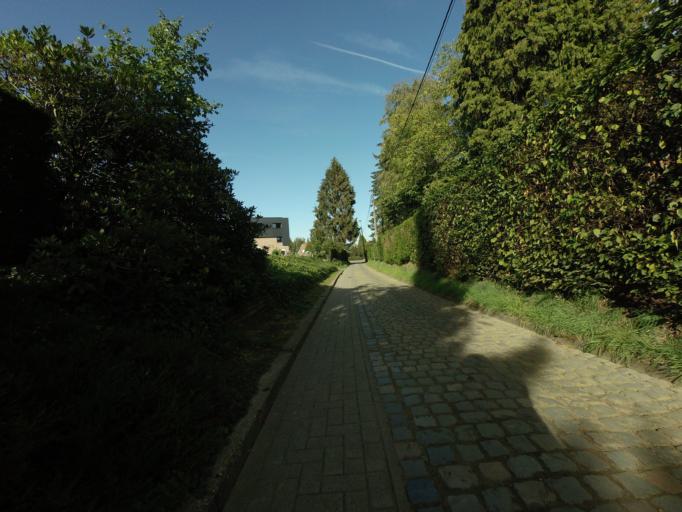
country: BE
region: Flanders
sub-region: Provincie Vlaams-Brabant
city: Herent
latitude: 50.8984
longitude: 4.6736
